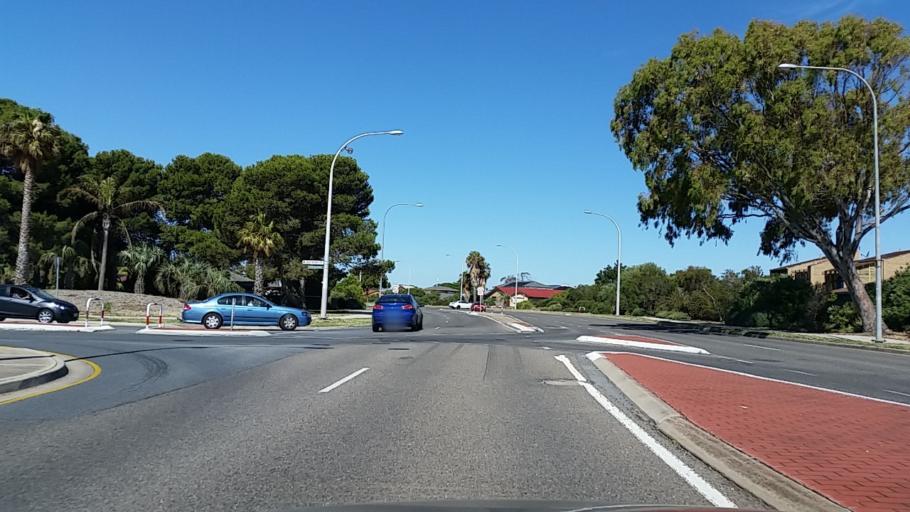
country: AU
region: South Australia
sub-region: Charles Sturt
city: Grange
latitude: -34.8943
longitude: 138.4926
